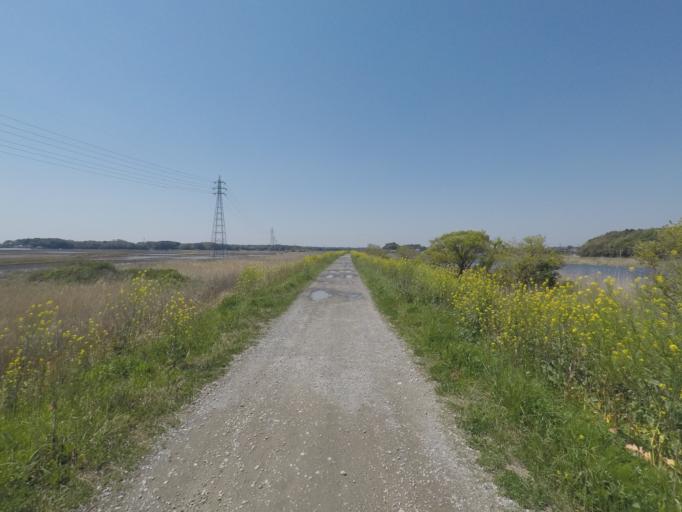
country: JP
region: Ibaraki
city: Ushiku
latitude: 35.9494
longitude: 140.1117
